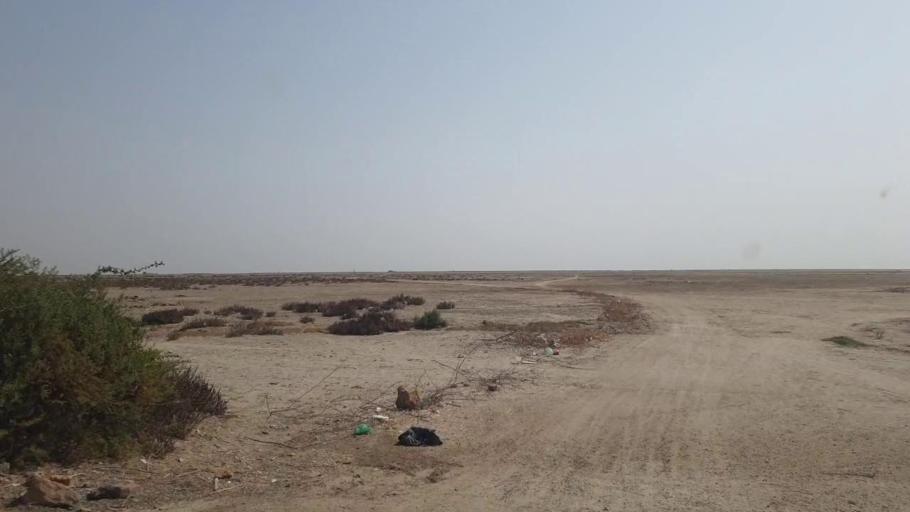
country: PK
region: Sindh
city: Jati
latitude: 24.3371
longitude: 68.6058
